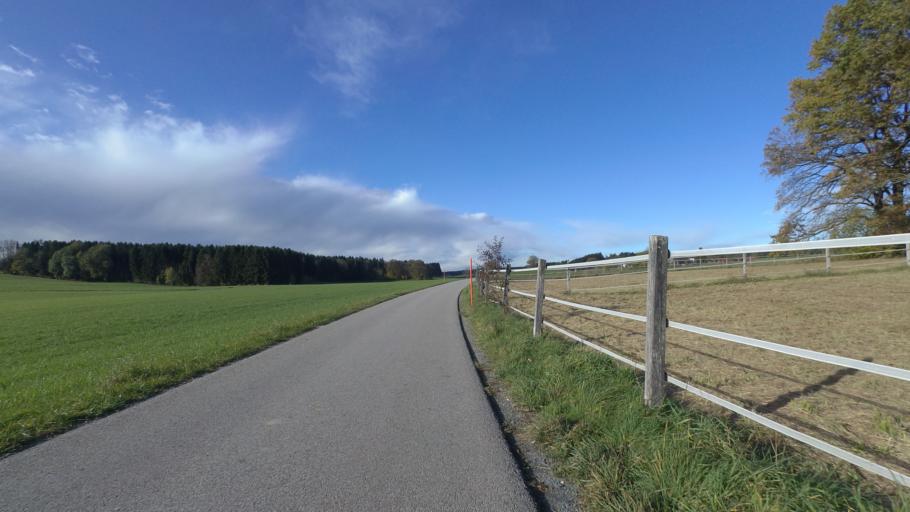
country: DE
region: Bavaria
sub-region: Upper Bavaria
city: Nussdorf
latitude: 47.9222
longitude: 12.5728
